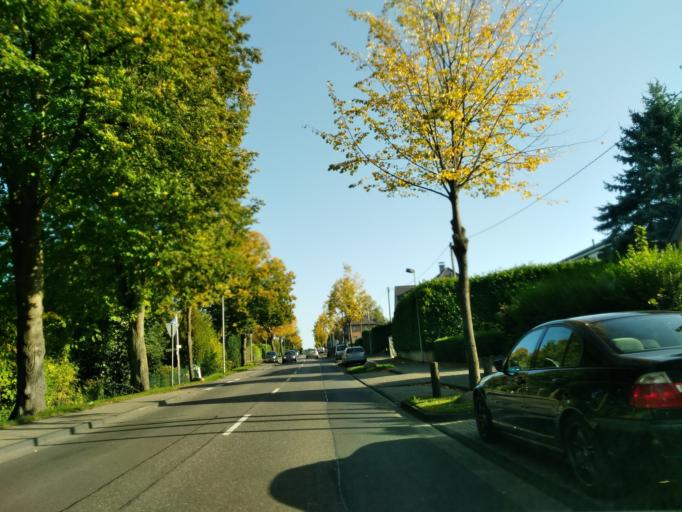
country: DE
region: North Rhine-Westphalia
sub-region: Regierungsbezirk Koln
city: Hennef
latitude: 50.7418
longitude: 7.3522
